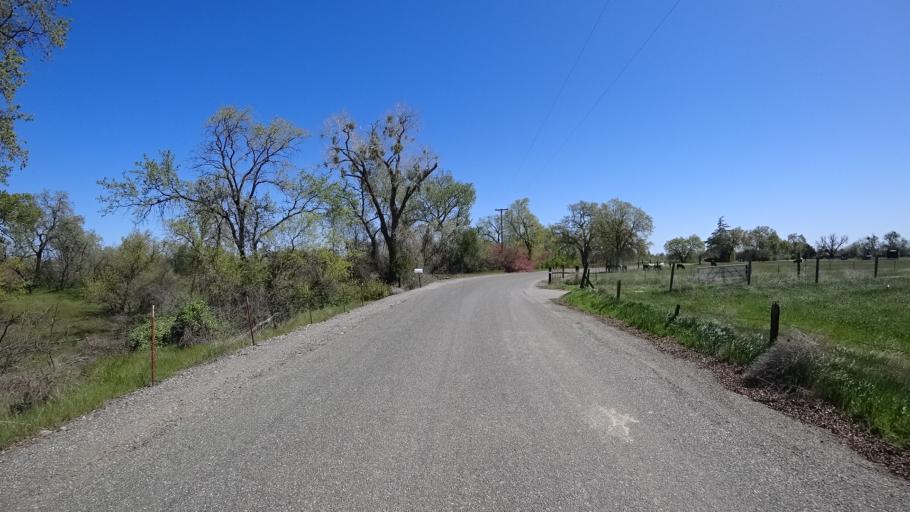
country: US
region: California
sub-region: Glenn County
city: Orland
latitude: 39.7841
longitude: -122.2408
